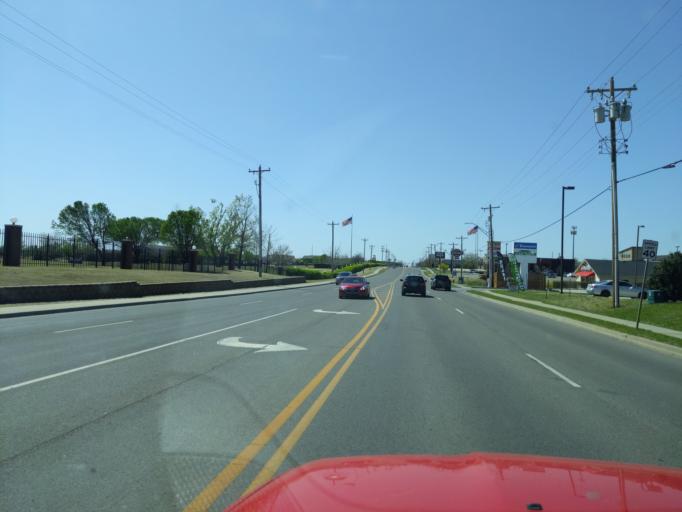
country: US
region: Oklahoma
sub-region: Cleveland County
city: Moore
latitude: 35.3198
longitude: -97.5045
